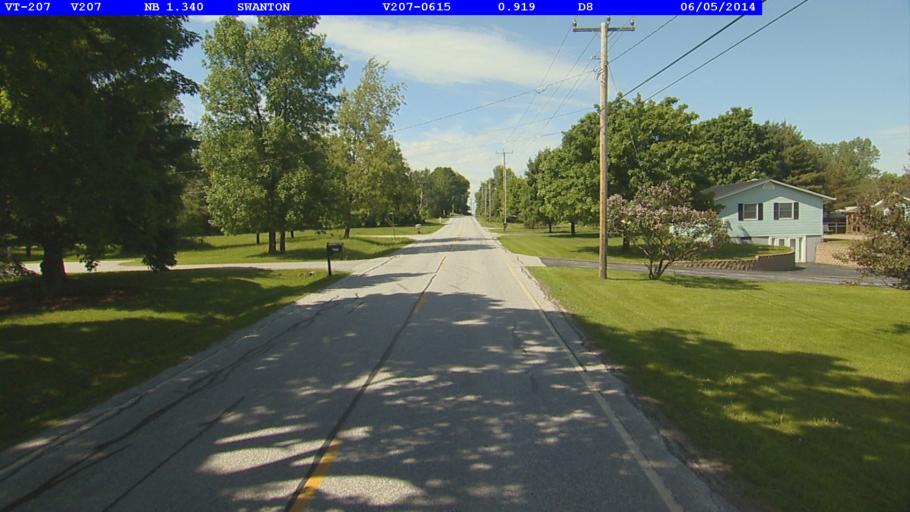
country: US
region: Vermont
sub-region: Franklin County
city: Saint Albans
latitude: 44.8582
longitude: -73.0749
